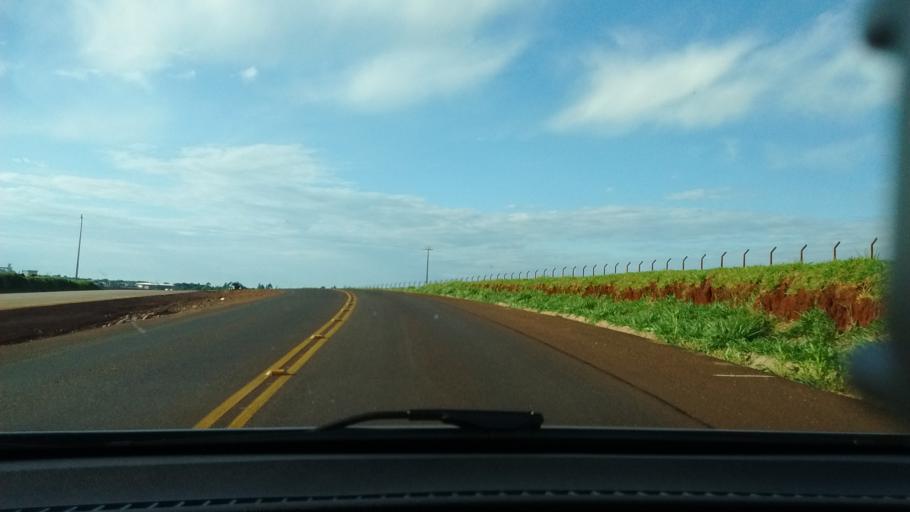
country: BR
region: Parana
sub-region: Cascavel
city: Cascavel
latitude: -25.1269
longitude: -53.5882
